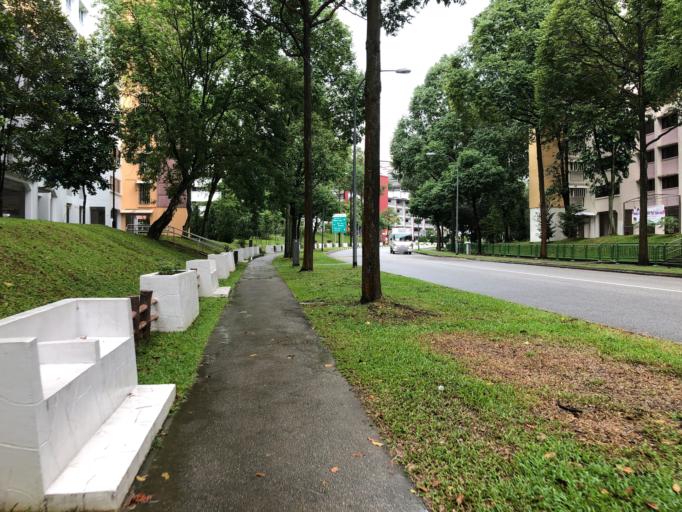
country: SG
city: Singapore
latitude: 1.3493
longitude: 103.7563
